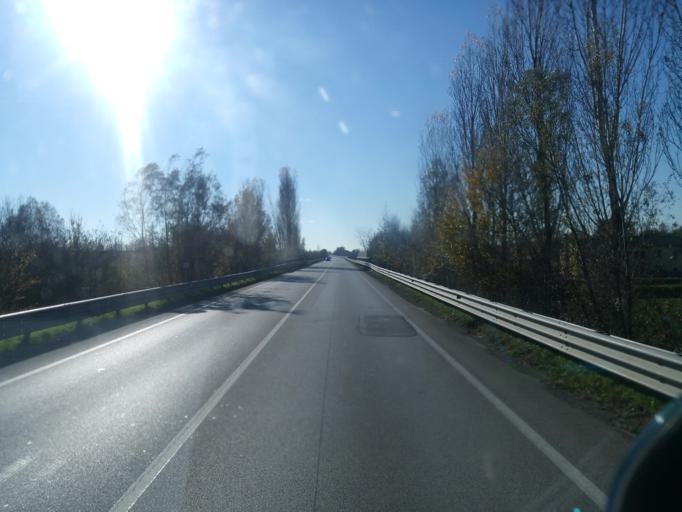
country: IT
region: Veneto
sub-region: Provincia di Padova
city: Camposampiero
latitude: 45.5686
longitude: 11.9539
